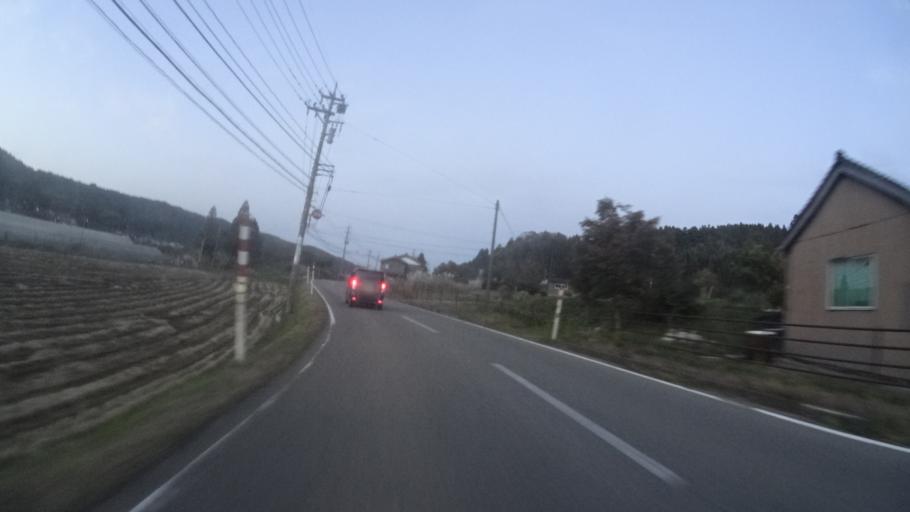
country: JP
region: Ishikawa
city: Nanao
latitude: 37.3700
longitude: 136.8753
